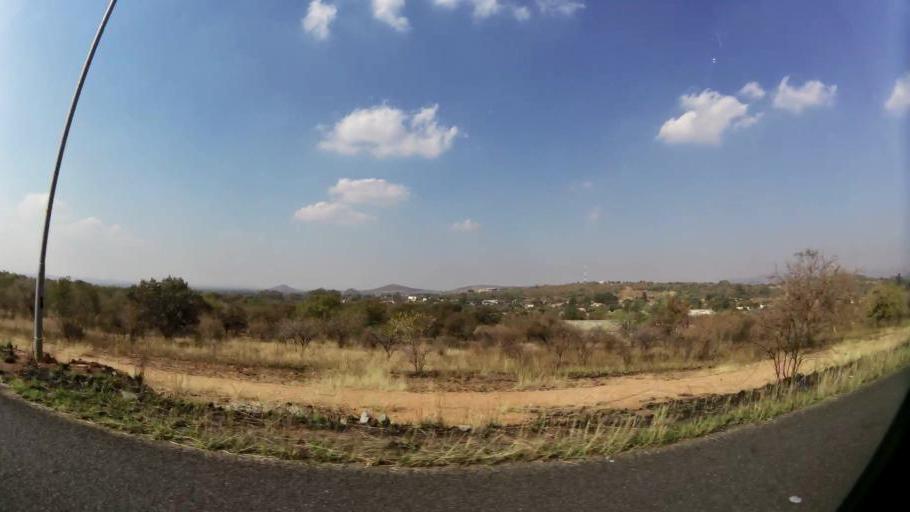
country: ZA
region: North-West
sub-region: Bojanala Platinum District Municipality
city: Rustenburg
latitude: -25.5737
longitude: 27.1395
